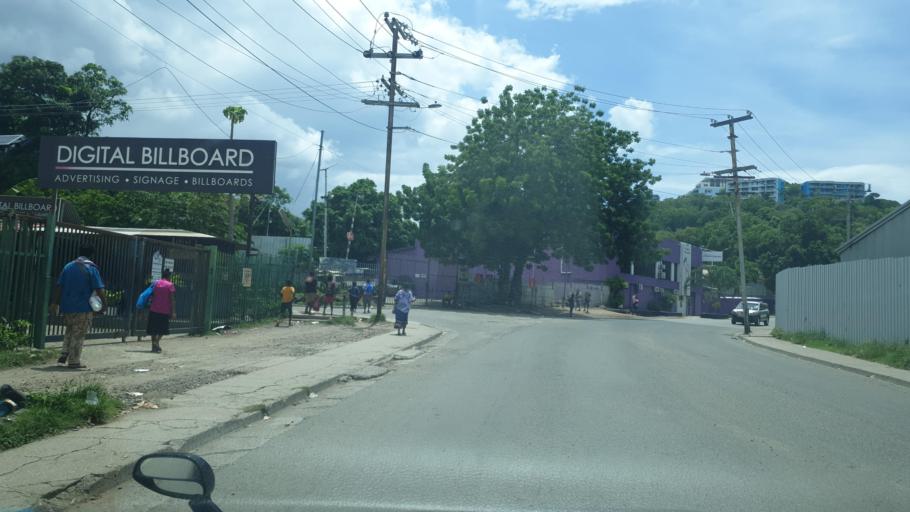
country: PG
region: National Capital
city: Port Moresby
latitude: -9.4683
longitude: 147.1600
